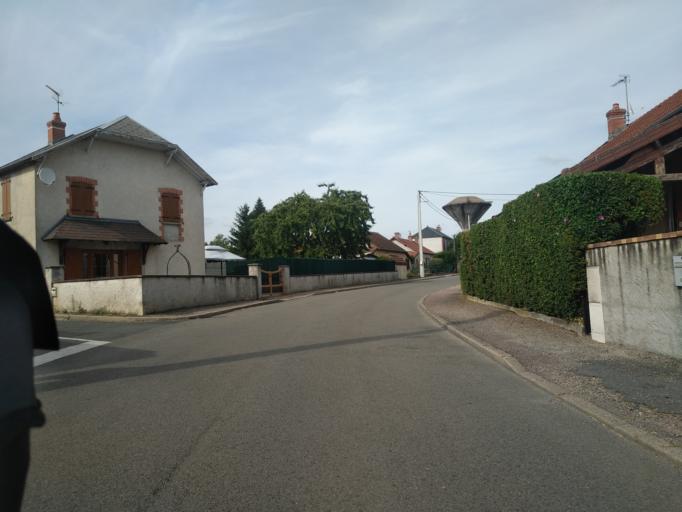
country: FR
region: Bourgogne
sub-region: Departement de Saone-et-Loire
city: Bourbon-Lancy
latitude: 46.6282
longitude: 3.7550
